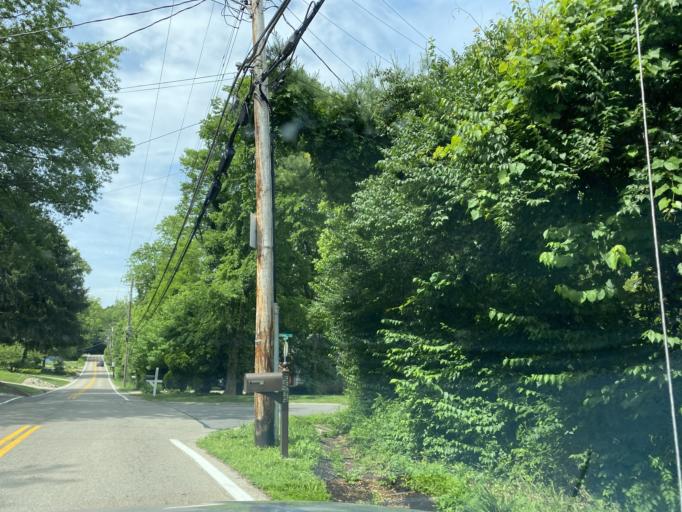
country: US
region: Ohio
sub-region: Hamilton County
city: Salem Heights
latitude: 39.0868
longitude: -84.4056
